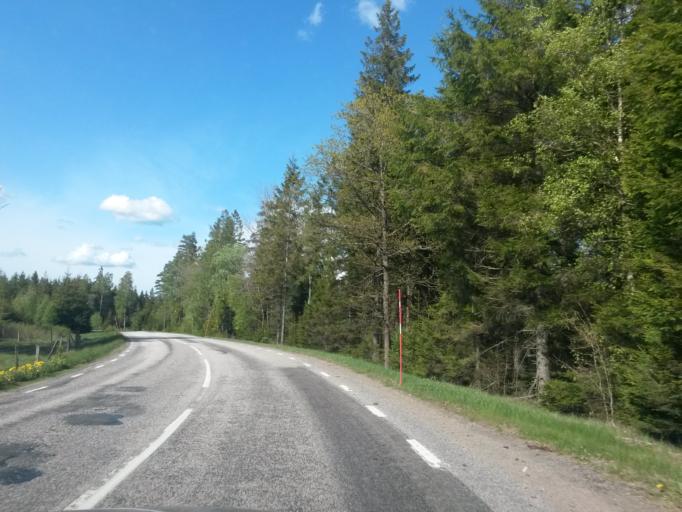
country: SE
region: Vaestra Goetaland
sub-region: Herrljunga Kommun
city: Herrljunga
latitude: 57.9602
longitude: 13.0046
